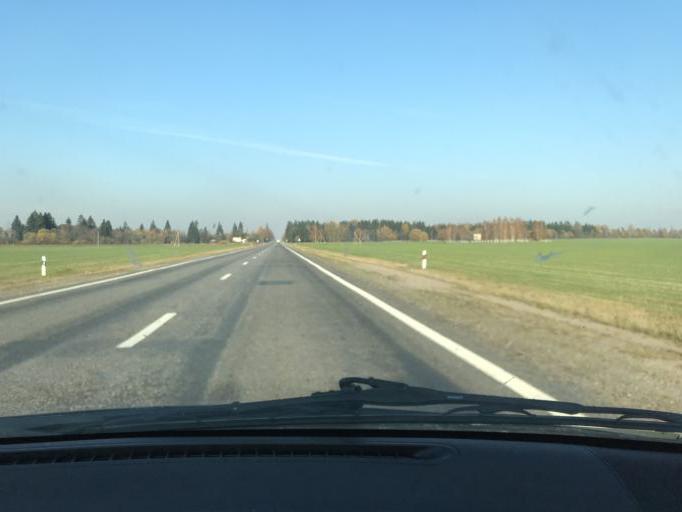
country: BY
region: Vitebsk
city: Orsha
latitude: 54.4469
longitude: 30.4892
